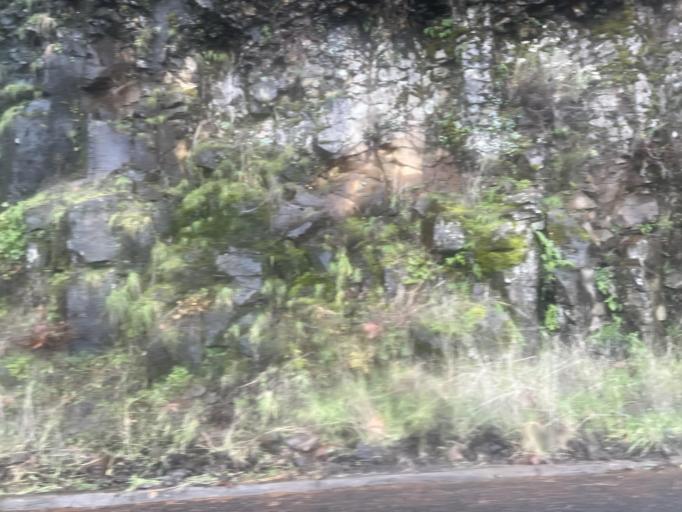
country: US
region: Washington
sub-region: Clark County
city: Washougal
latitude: 45.5480
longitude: -122.1965
